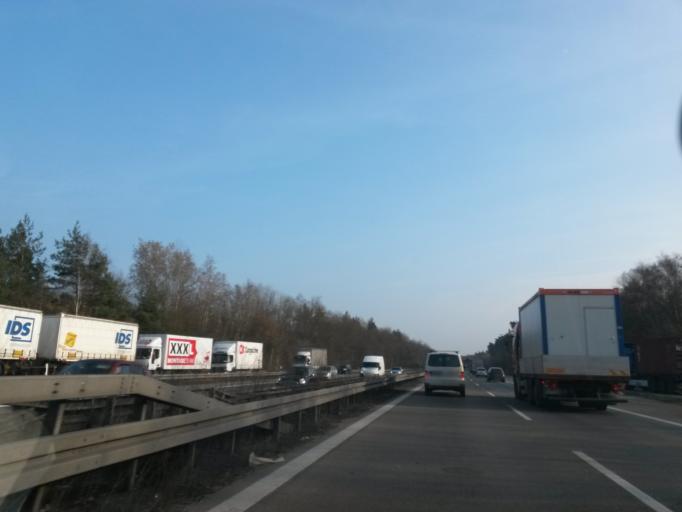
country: DE
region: Bavaria
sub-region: Regierungsbezirk Mittelfranken
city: Nuernberg
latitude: 49.4063
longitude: 11.0716
